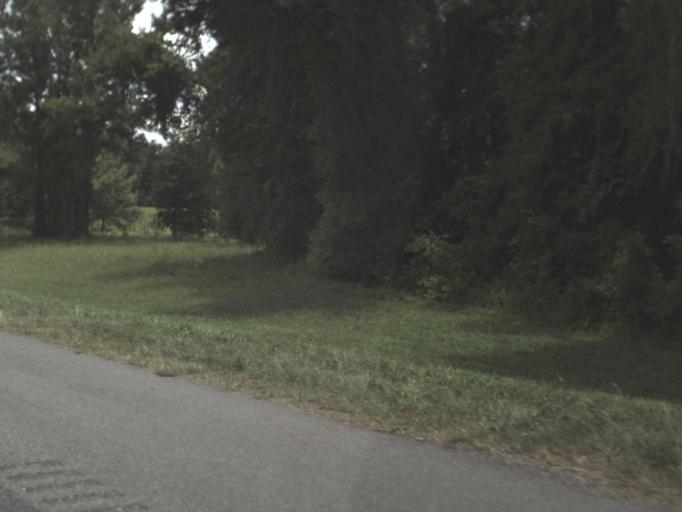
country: US
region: Florida
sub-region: Alachua County
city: High Springs
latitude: 29.9542
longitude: -82.5697
